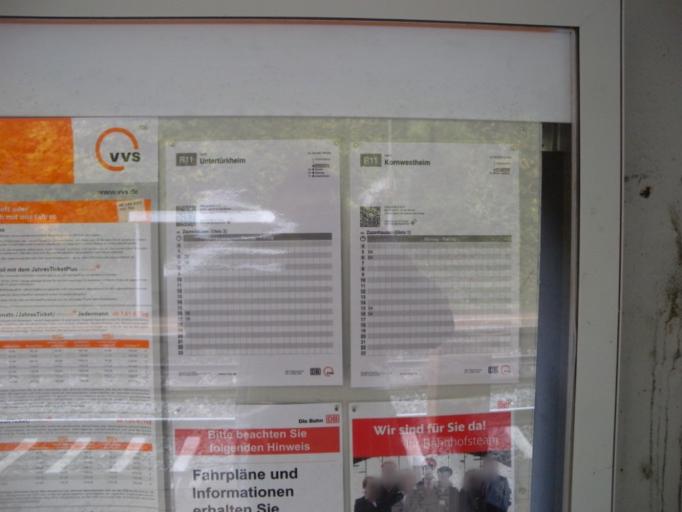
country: DE
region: Baden-Wuerttemberg
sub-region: Regierungsbezirk Stuttgart
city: Kornwestheim
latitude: 48.8360
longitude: 9.1995
